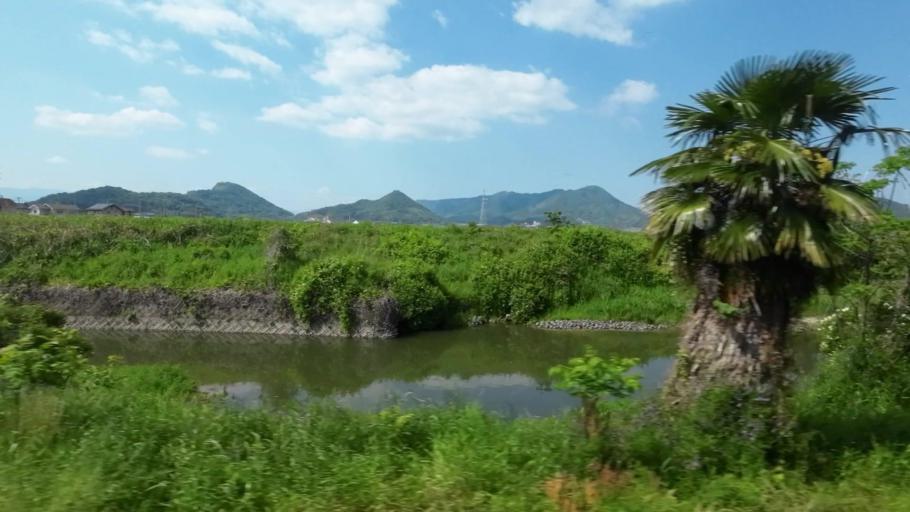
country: JP
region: Kagawa
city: Tadotsu
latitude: 34.2118
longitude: 133.7066
